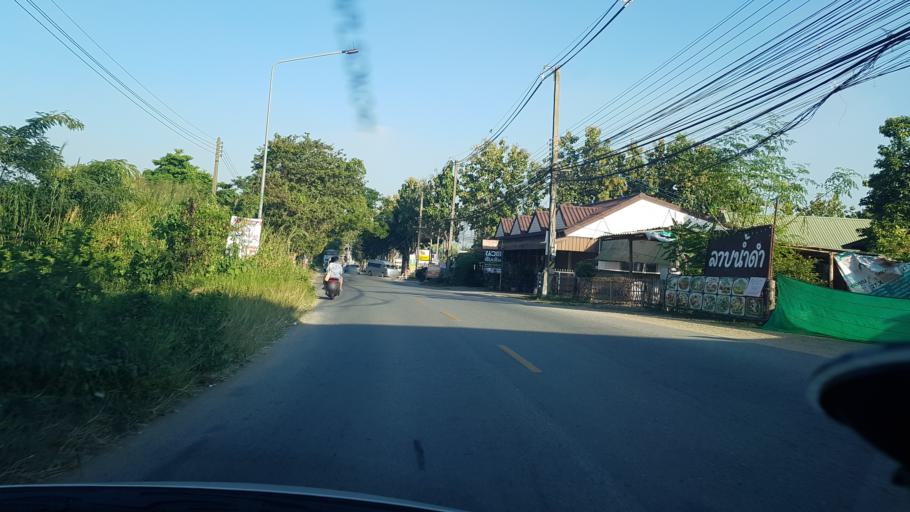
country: TH
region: Chiang Rai
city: Chiang Rai
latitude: 19.9290
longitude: 99.8288
